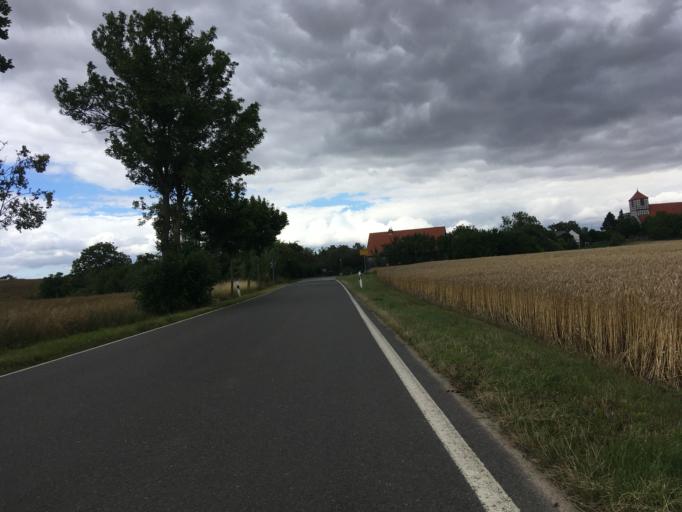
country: DE
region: Brandenburg
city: Gramzow
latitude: 53.2417
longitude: 13.9377
